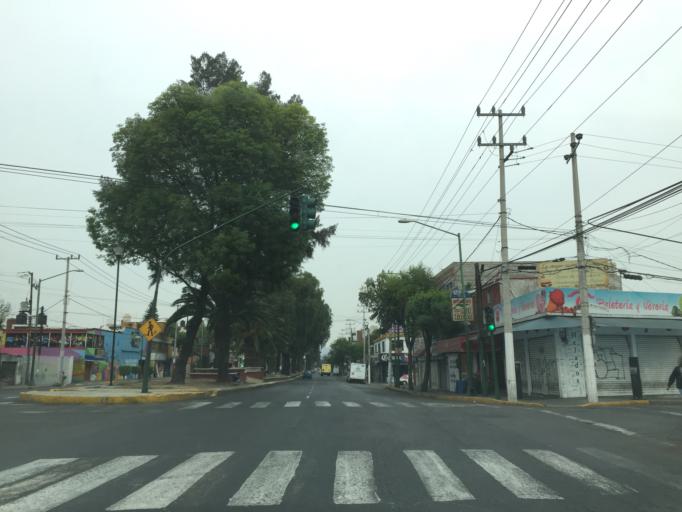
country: MX
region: Mexico
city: Colonia Lindavista
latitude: 19.4985
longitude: -99.1244
